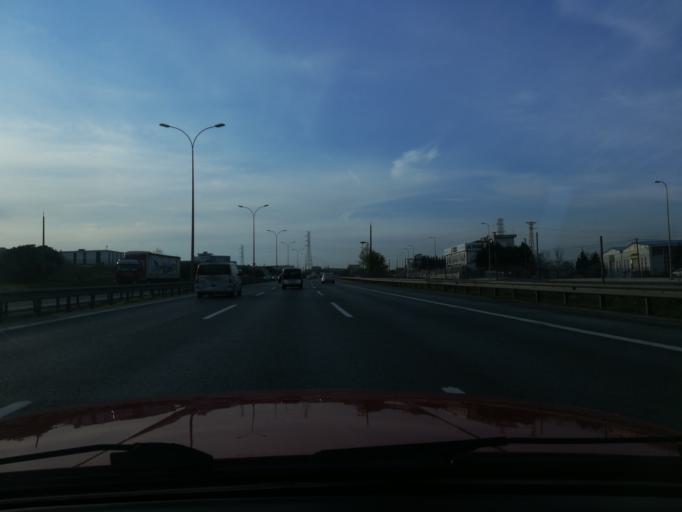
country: TR
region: Kocaeli
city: Balcik
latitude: 40.9059
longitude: 29.3627
